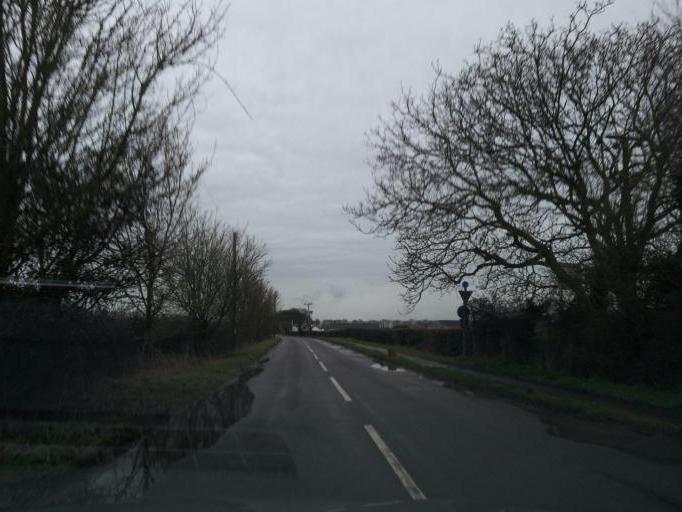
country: GB
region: England
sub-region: Cambridgeshire
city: Bottisham
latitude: 52.2365
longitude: 0.2483
